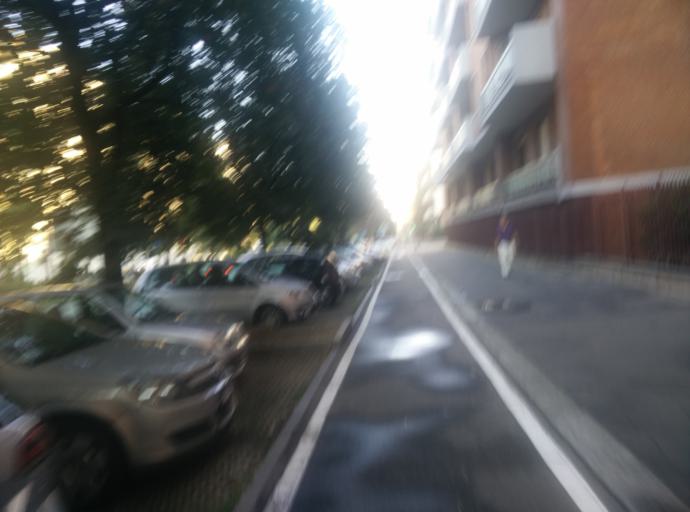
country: IT
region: Piedmont
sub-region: Provincia di Torino
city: Lesna
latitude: 45.0372
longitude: 7.6384
